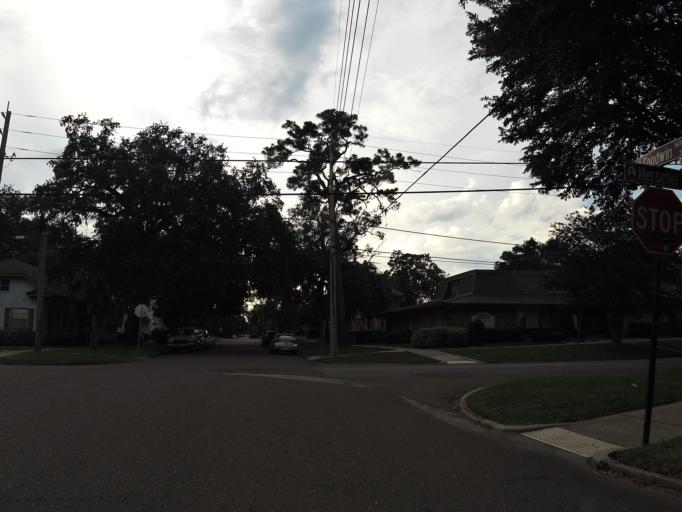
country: US
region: Florida
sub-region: Duval County
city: Jacksonville
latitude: 30.3124
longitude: -81.6828
